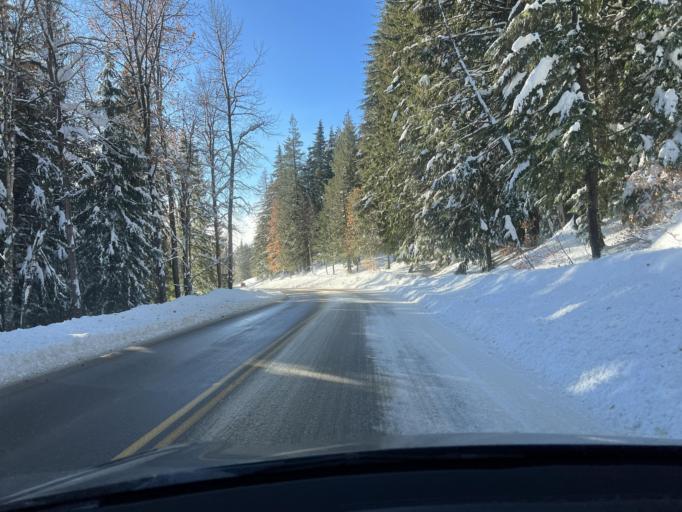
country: US
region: Idaho
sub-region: Bonner County
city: Ponderay
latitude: 48.3437
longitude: -116.5994
